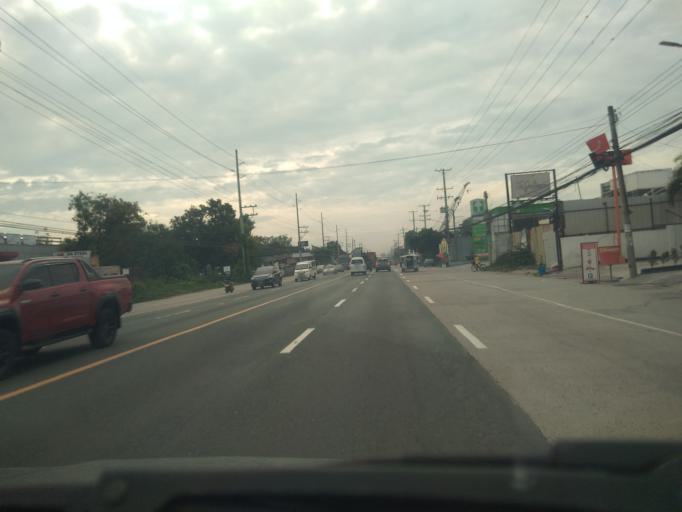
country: PH
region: Central Luzon
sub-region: Province of Pampanga
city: Bulaon
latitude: 15.0619
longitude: 120.6545
